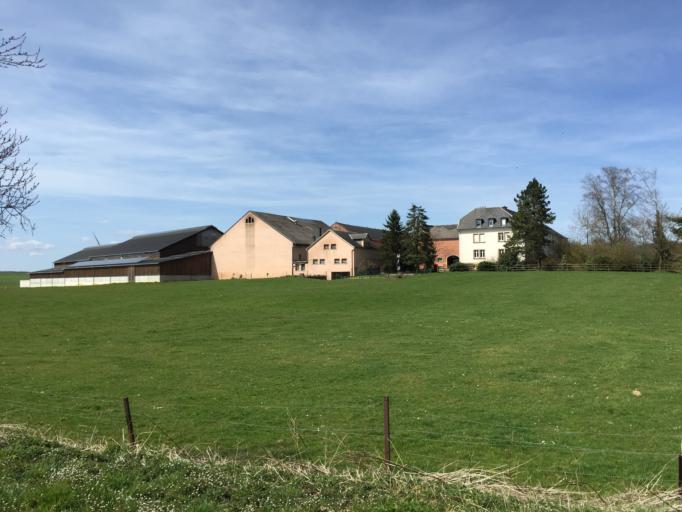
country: LU
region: Luxembourg
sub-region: Canton de Capellen
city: Clemency
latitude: 49.6292
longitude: 5.8923
